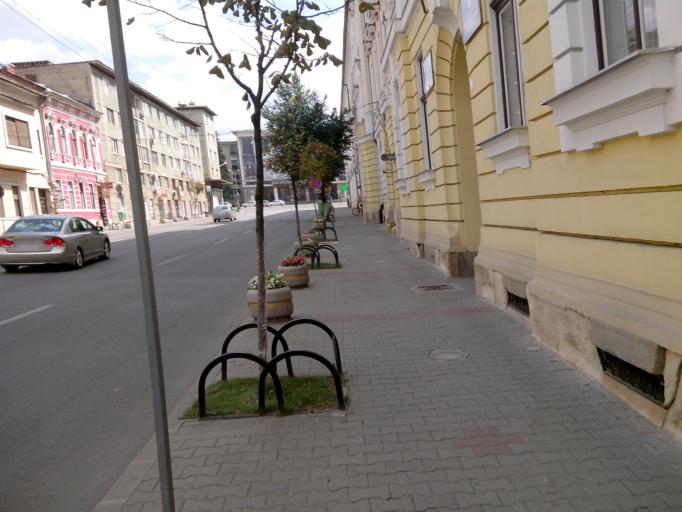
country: RO
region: Cluj
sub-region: Municipiul Cluj-Napoca
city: Cluj-Napoca
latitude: 46.7685
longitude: 23.5851
